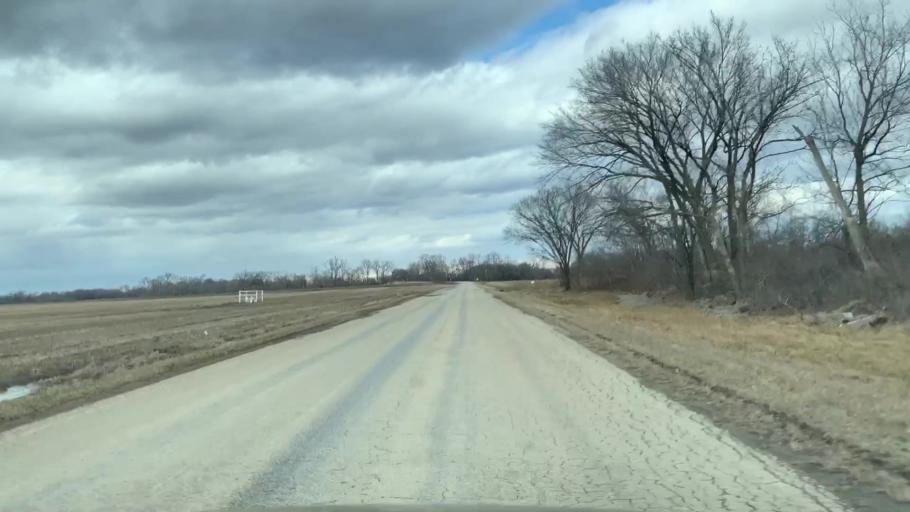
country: US
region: Kansas
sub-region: Allen County
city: Humboldt
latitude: 37.7974
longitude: -95.4706
